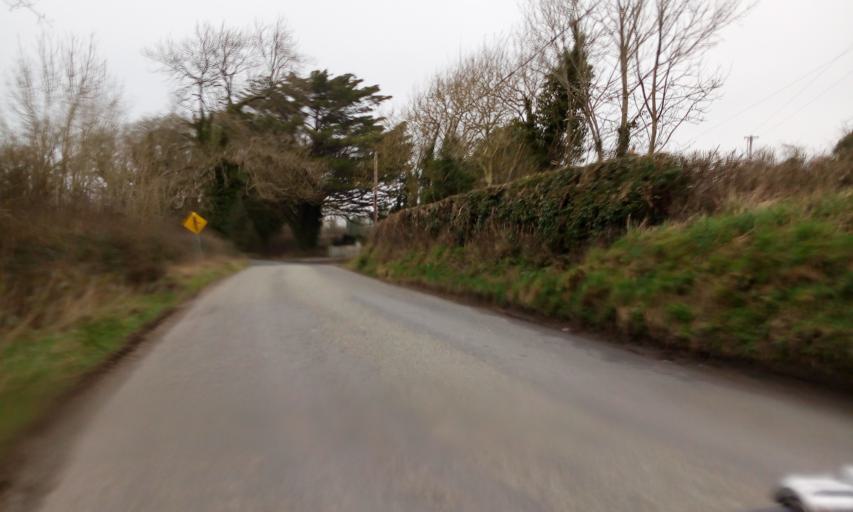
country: IE
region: Leinster
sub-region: Kilkenny
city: Kilkenny
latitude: 52.6587
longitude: -7.1862
